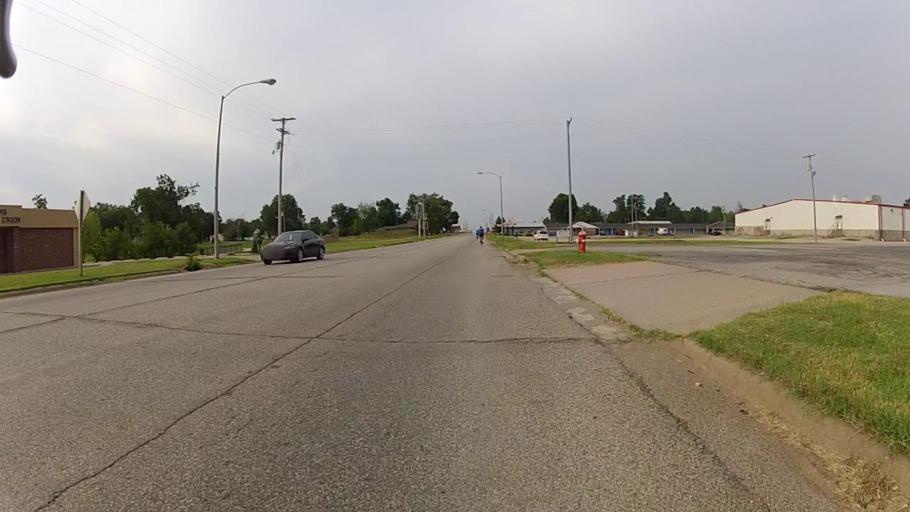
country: US
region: Kansas
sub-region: Cherokee County
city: Columbus
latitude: 37.1755
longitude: -94.8318
